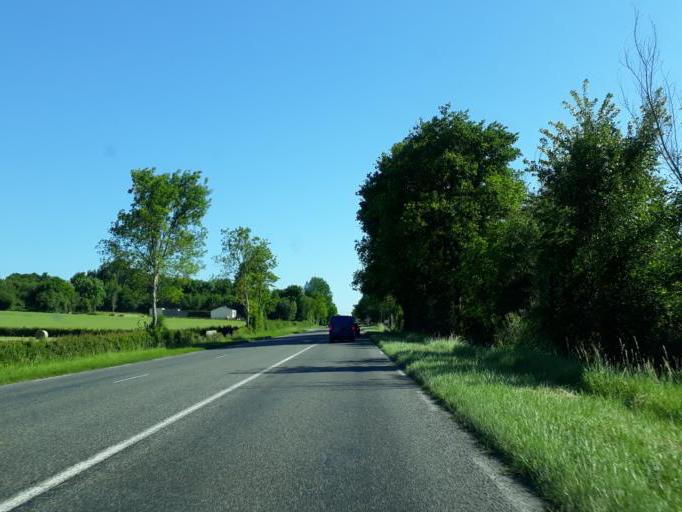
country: FR
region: Bourgogne
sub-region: Departement de la Nievre
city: Cosne-Cours-sur-Loire
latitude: 47.4560
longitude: 2.9315
